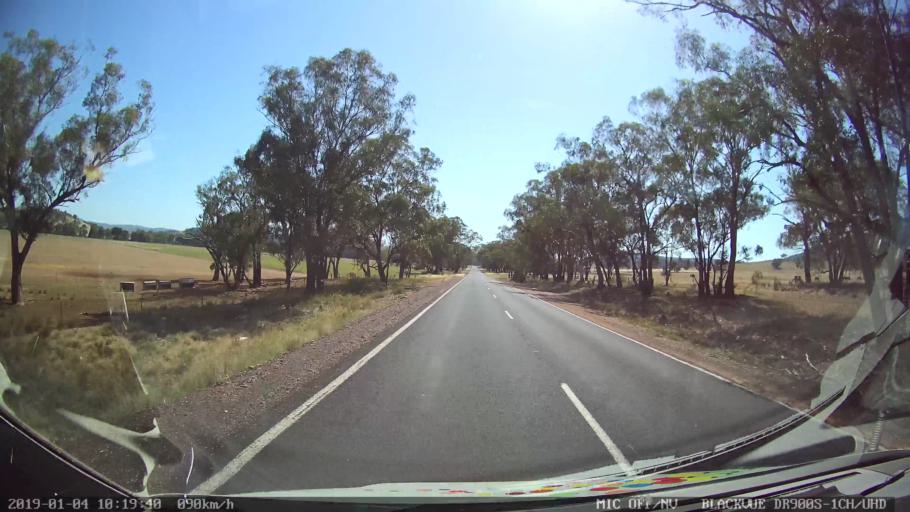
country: AU
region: New South Wales
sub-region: Cabonne
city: Canowindra
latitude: -33.3756
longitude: 148.4841
